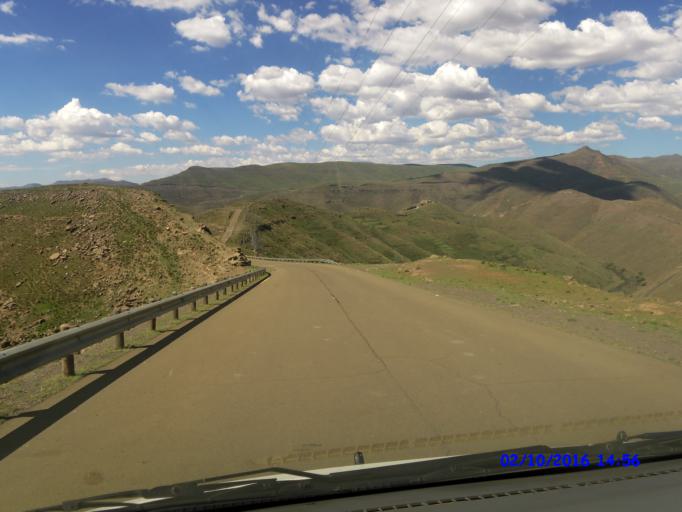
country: LS
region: Maseru
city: Nako
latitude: -29.4690
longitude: 28.0902
